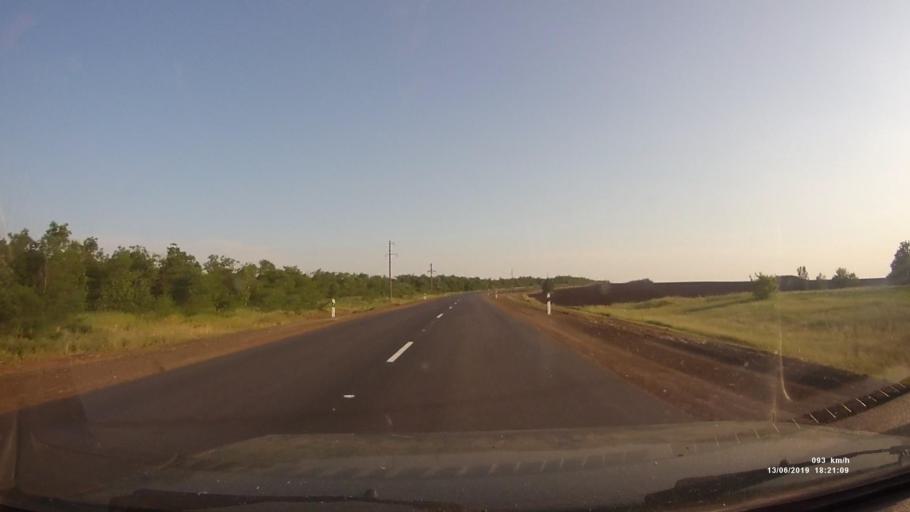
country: RU
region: Rostov
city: Kazanskaya
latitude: 49.8744
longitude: 41.2942
